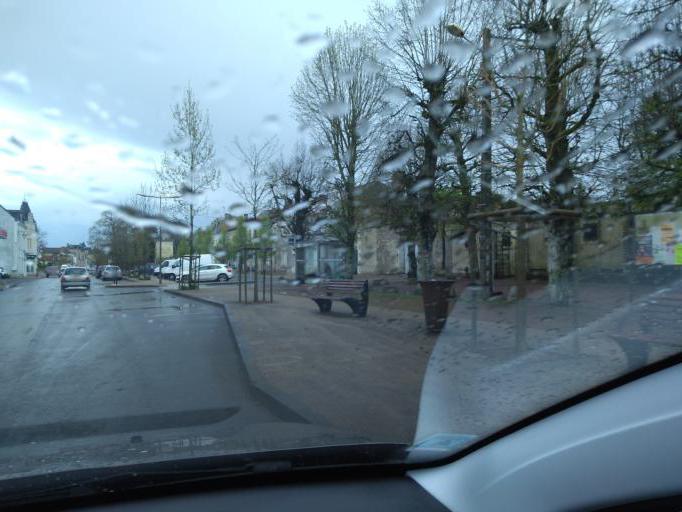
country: FR
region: Poitou-Charentes
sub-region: Departement de la Vienne
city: Loudun
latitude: 47.0128
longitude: 0.0821
